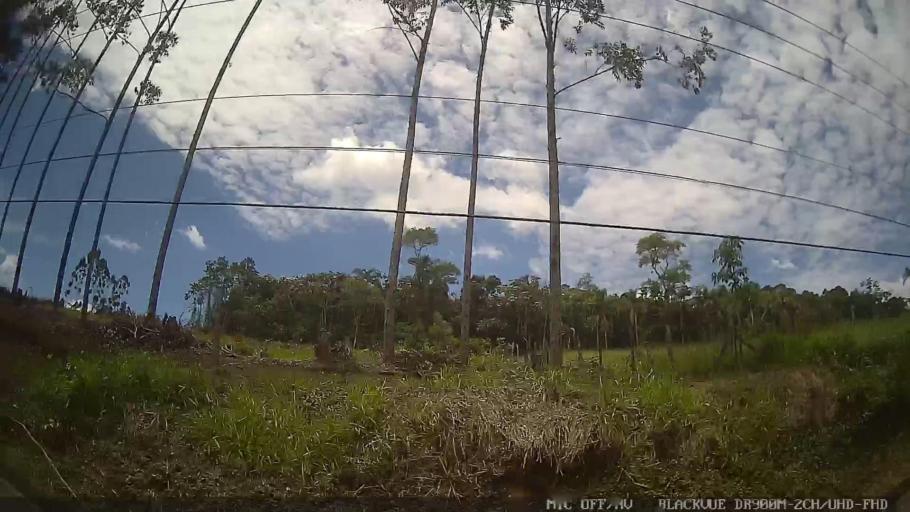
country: BR
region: Sao Paulo
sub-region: Biritiba-Mirim
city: Biritiba Mirim
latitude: -23.5422
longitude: -45.9408
